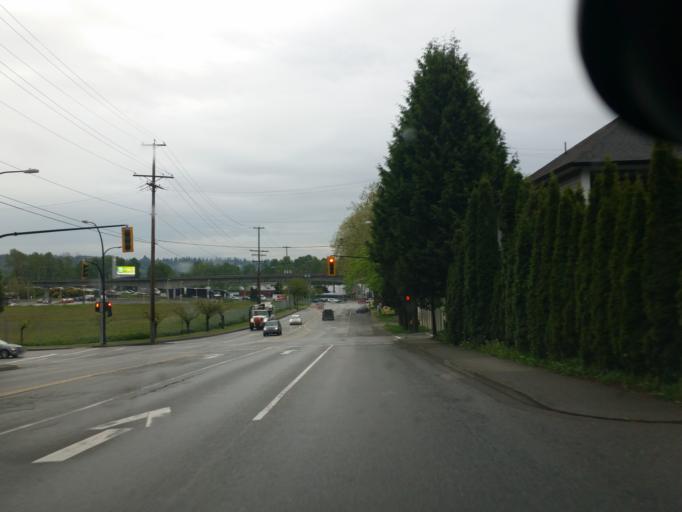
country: CA
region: British Columbia
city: New Westminster
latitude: 49.2315
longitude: -122.8871
